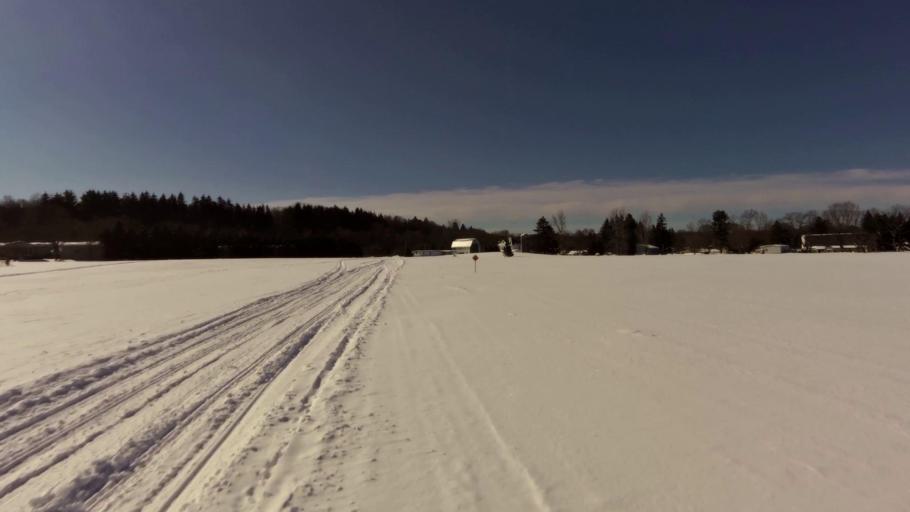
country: US
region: New York
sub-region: Cattaraugus County
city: Franklinville
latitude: 42.3455
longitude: -78.4481
